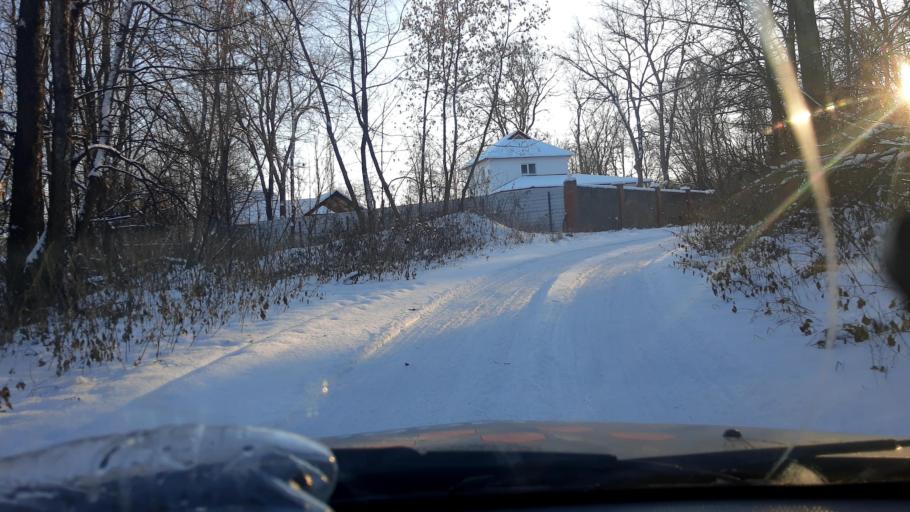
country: RU
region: Bashkortostan
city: Ufa
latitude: 54.6554
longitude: 55.9719
